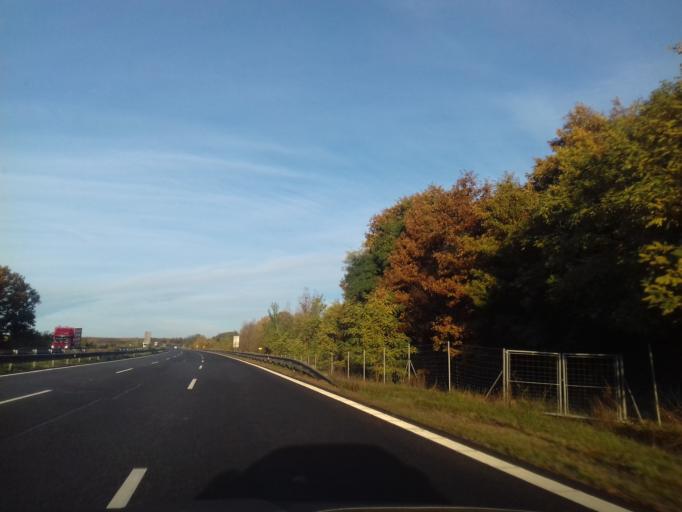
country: SK
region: Nitriansky
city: Tlmace
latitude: 48.3651
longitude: 18.5577
